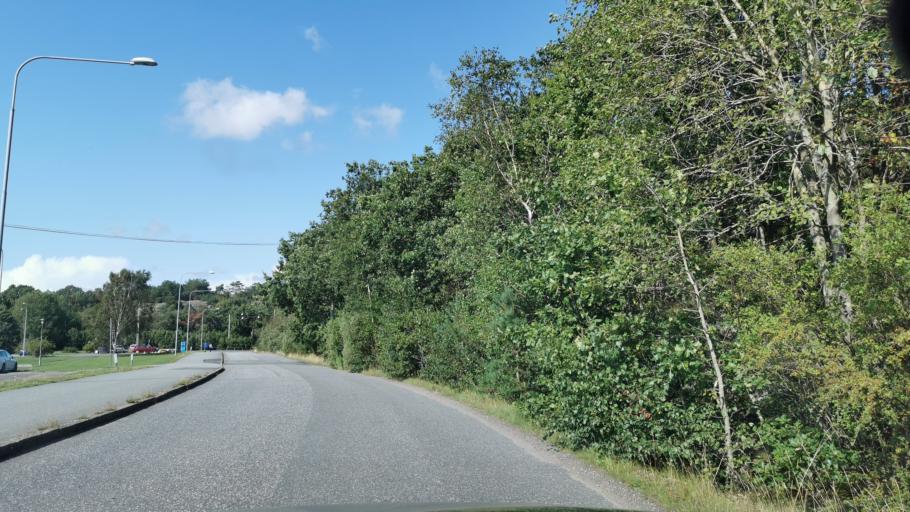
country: SE
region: Vaestra Goetaland
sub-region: Goteborg
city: Majorna
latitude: 57.6425
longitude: 11.9209
